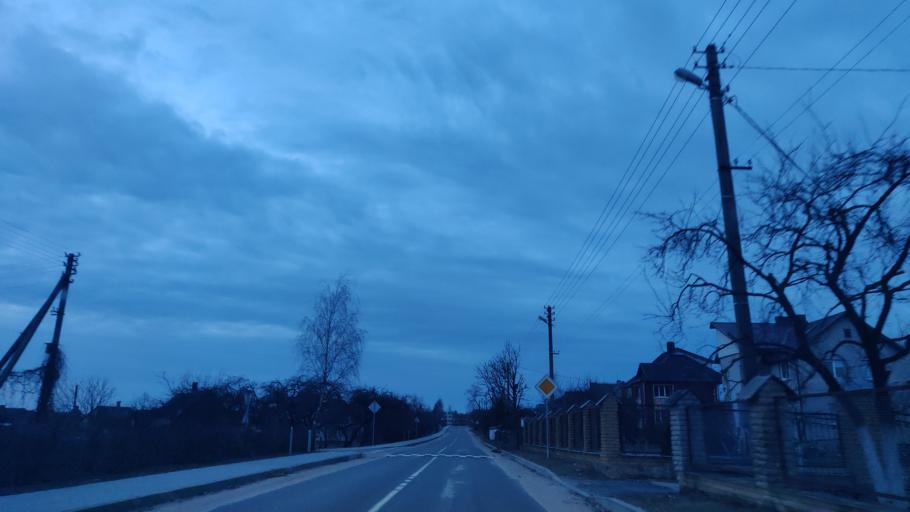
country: LT
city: Trakai
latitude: 54.6102
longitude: 24.9873
